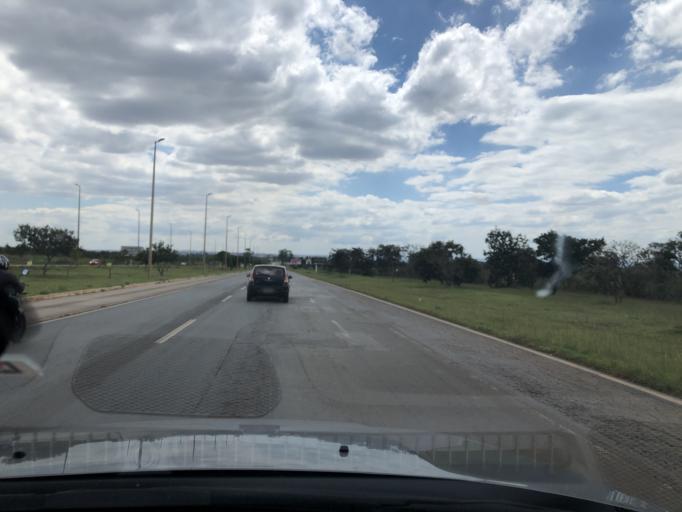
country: BR
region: Federal District
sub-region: Brasilia
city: Brasilia
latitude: -15.9652
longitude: -47.9920
